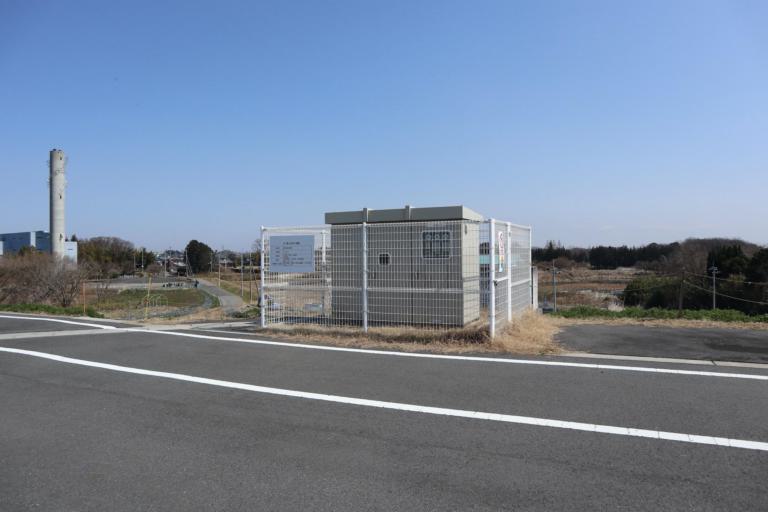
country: JP
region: Ibaraki
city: Koga
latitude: 36.1781
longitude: 139.6937
